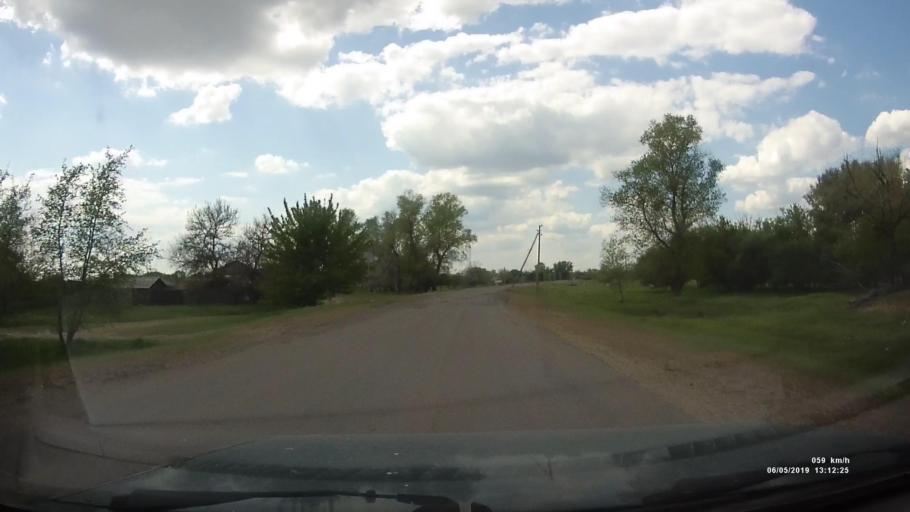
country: RU
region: Rostov
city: Ust'-Donetskiy
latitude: 47.7554
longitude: 40.9476
